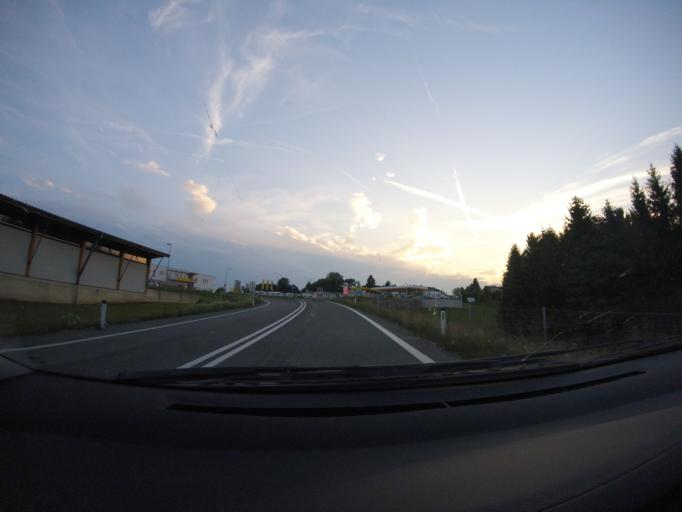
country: AT
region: Styria
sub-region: Politischer Bezirk Graz-Umgebung
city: Nestelbach bei Graz
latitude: 47.0629
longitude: 15.5927
